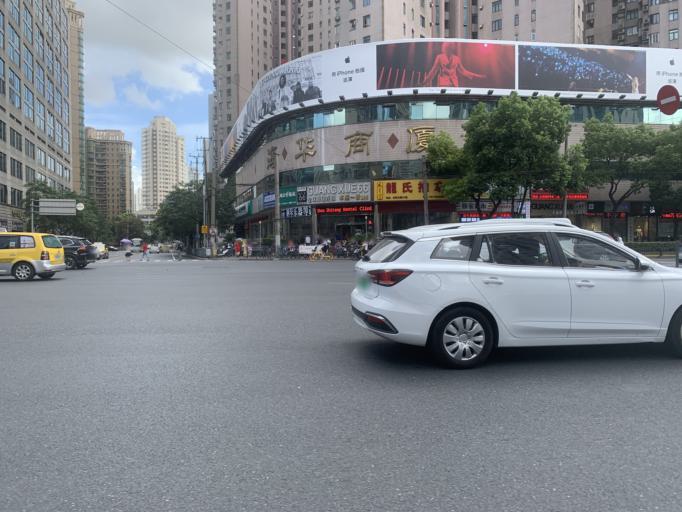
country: CN
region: Shanghai Shi
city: Luwan
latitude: 31.2075
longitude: 121.4649
